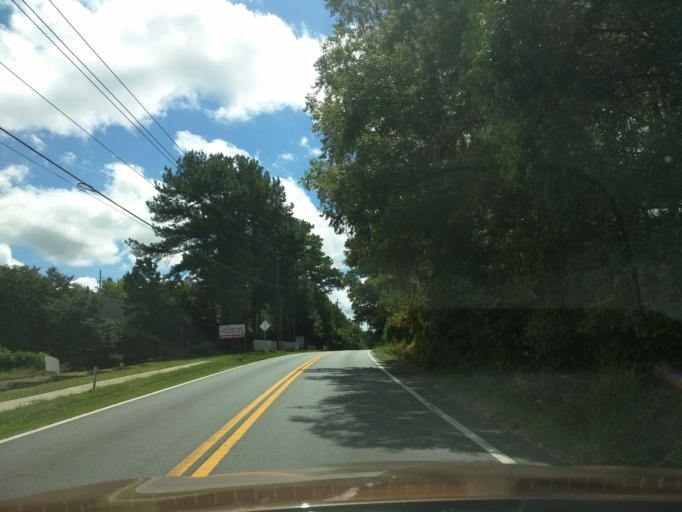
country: US
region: Florida
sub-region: Leon County
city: Tallahassee
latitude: 30.5867
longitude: -84.2515
